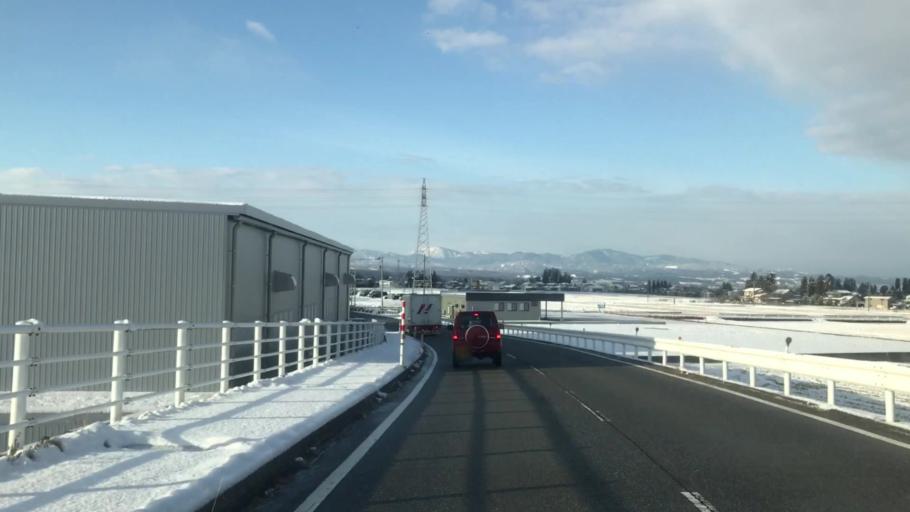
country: JP
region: Toyama
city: Kamiichi
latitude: 36.6235
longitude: 137.2926
